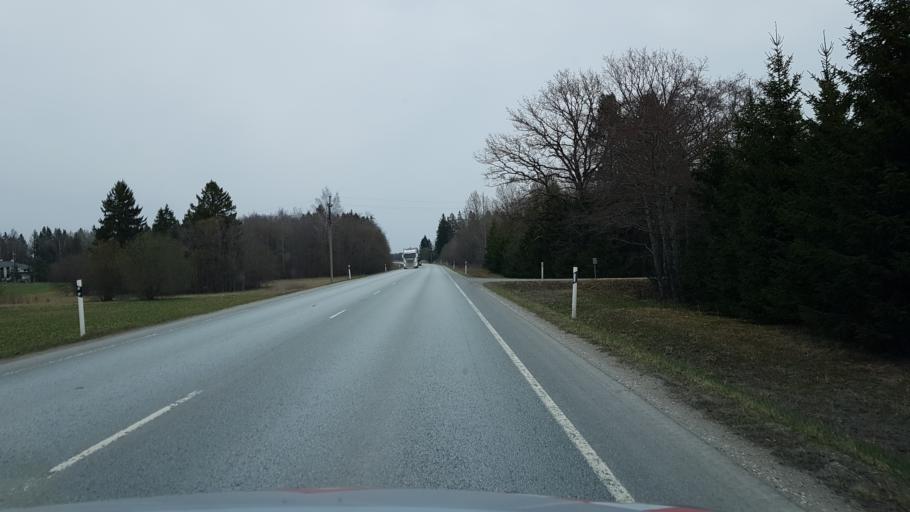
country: EE
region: Laeaene-Virumaa
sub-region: Rakvere linn
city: Rakvere
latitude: 59.3231
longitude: 26.3819
